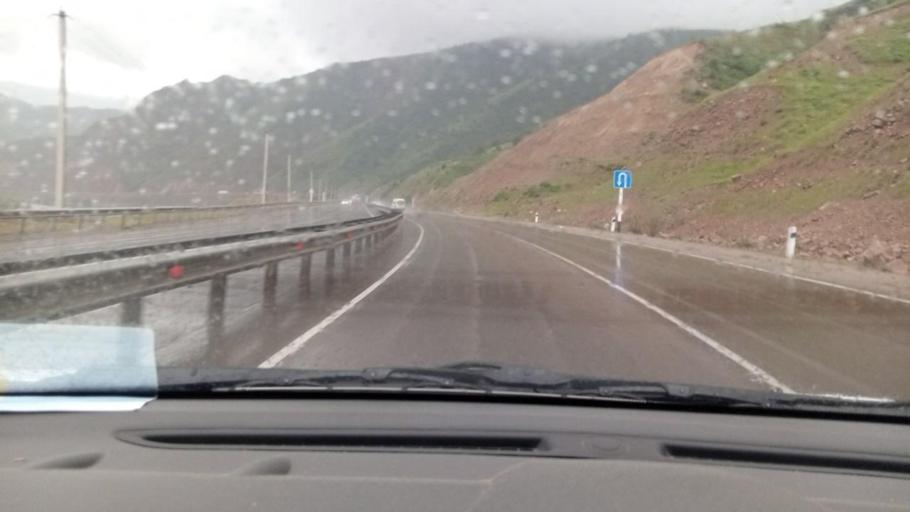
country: UZ
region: Toshkent
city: Angren
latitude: 41.0986
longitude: 70.3230
